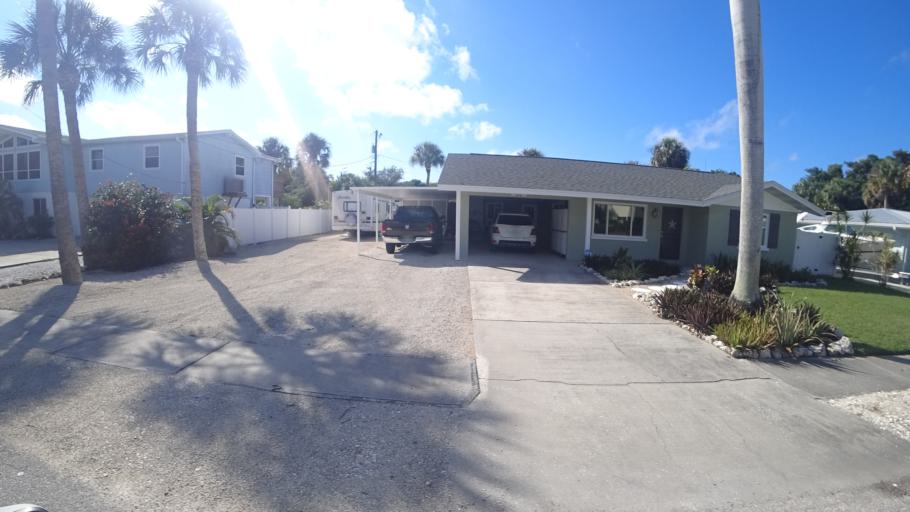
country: US
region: Florida
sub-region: Manatee County
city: Anna Maria
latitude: 27.5236
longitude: -82.7277
